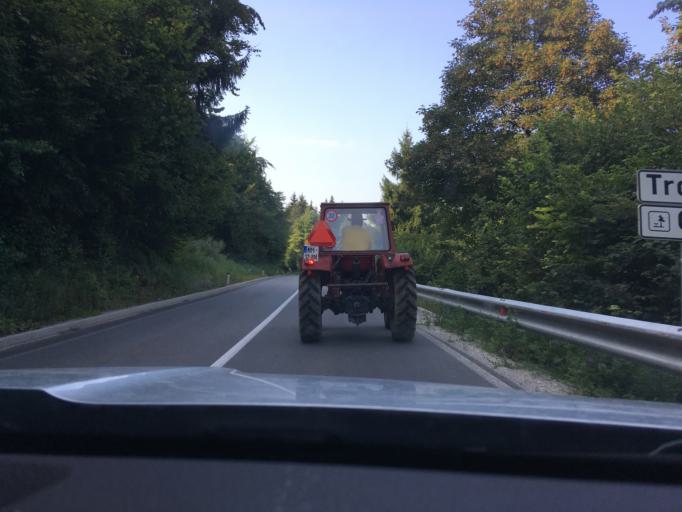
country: SI
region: Semic
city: Semic
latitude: 45.7237
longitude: 15.2338
